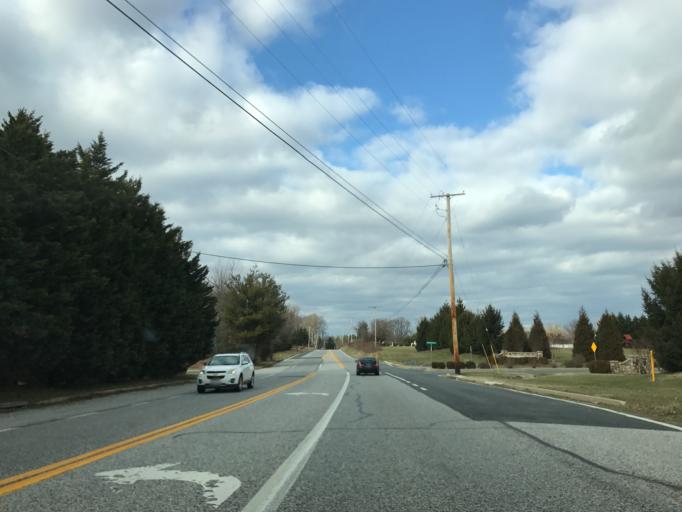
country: US
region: Maryland
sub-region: Harford County
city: South Bel Air
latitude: 39.5679
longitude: -76.2539
